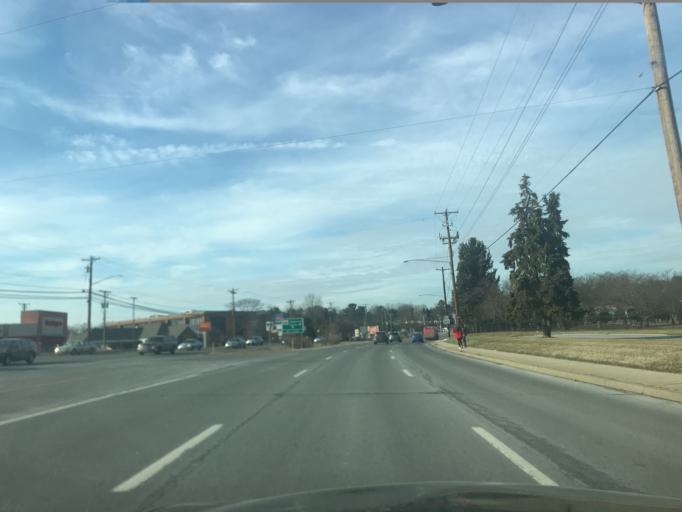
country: US
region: Maryland
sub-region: Montgomery County
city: Aspen Hill
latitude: 39.0817
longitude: -77.0761
